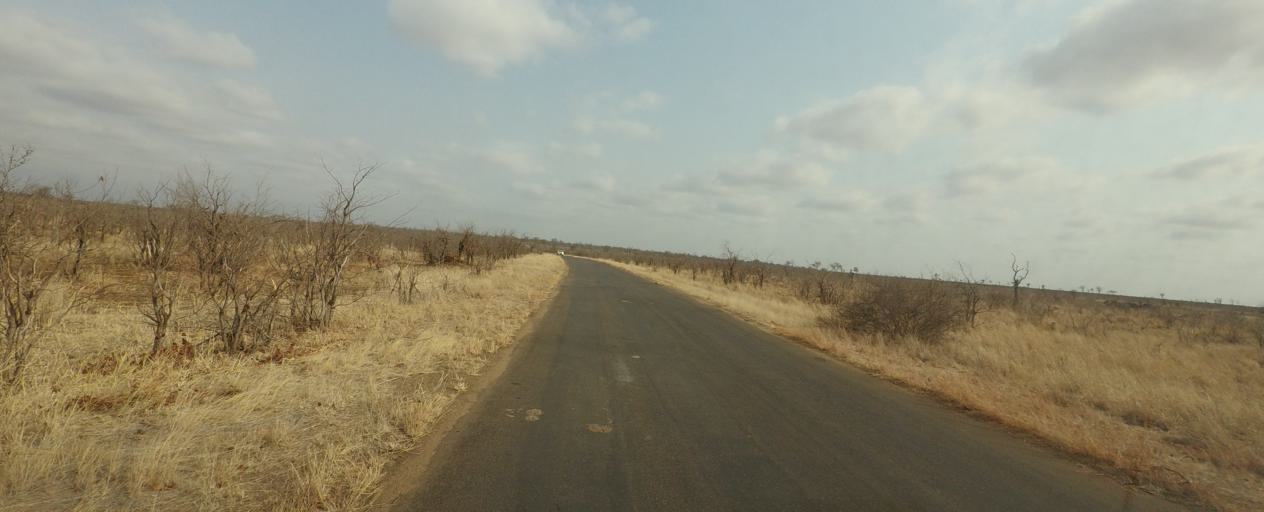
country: ZA
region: Limpopo
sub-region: Vhembe District Municipality
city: Mutale
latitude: -22.8970
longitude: 31.2515
